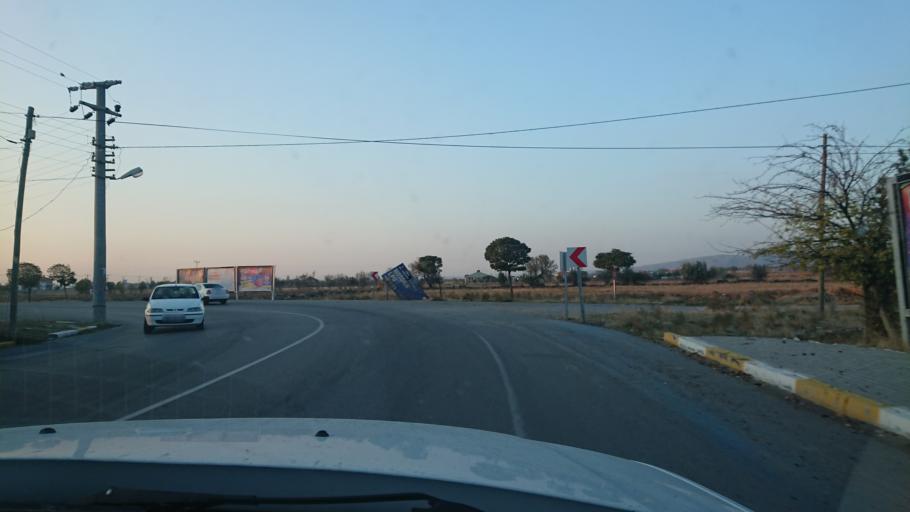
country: TR
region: Aksaray
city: Aksaray
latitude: 38.3095
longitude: 34.0662
